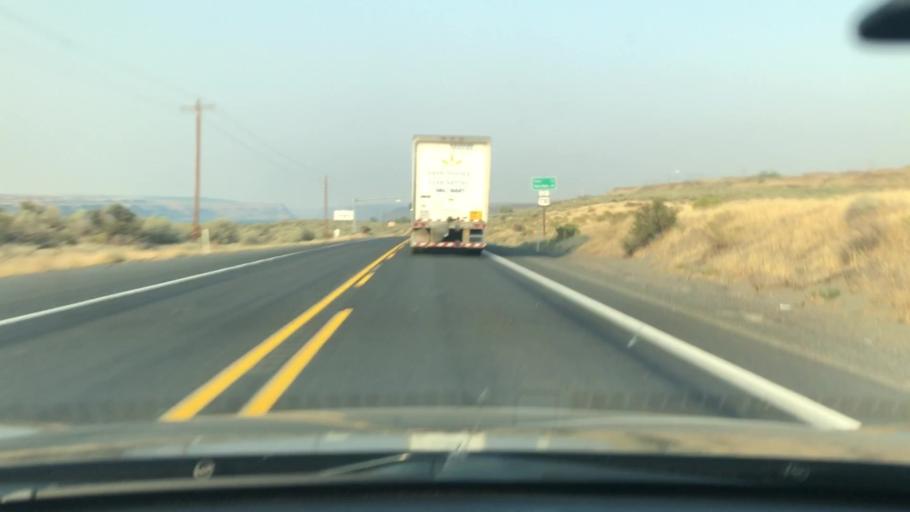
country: US
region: Oregon
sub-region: Umatilla County
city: Stanfield
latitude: 45.9165
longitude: -119.1321
